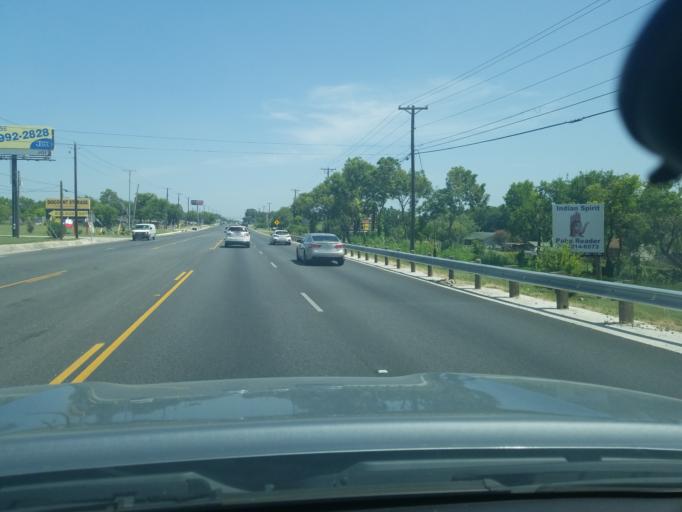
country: US
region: Texas
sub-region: Guadalupe County
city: Lake Dunlap
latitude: 29.6817
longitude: -98.0636
